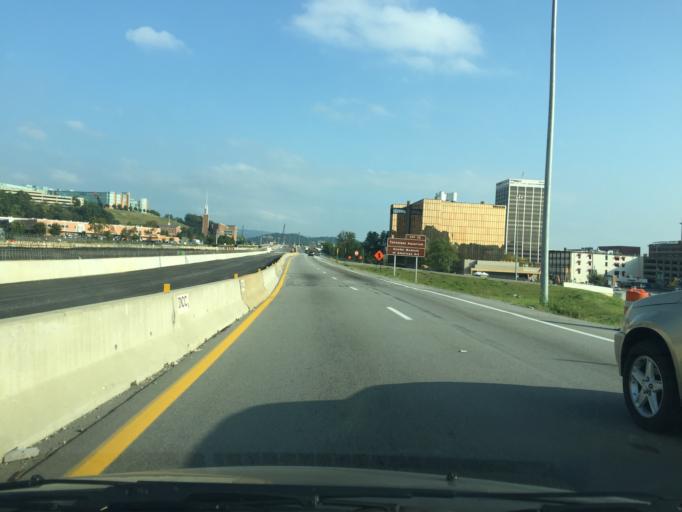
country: US
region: Tennessee
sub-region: Hamilton County
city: Chattanooga
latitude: 35.0441
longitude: -85.3139
